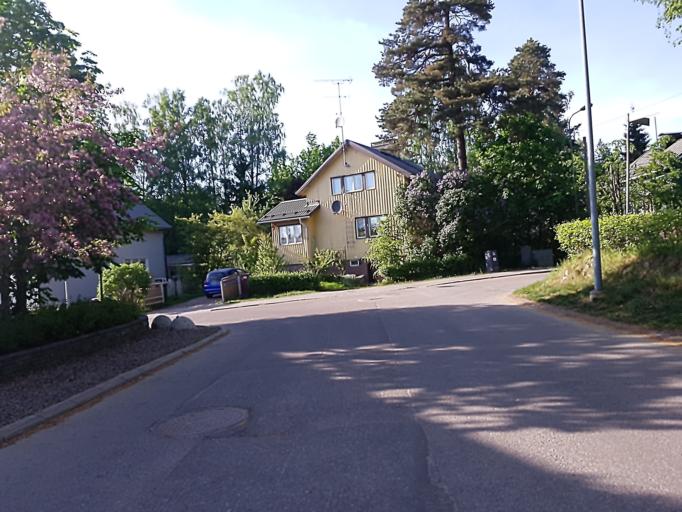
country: FI
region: Uusimaa
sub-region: Helsinki
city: Helsinki
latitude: 60.2411
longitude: 24.9391
